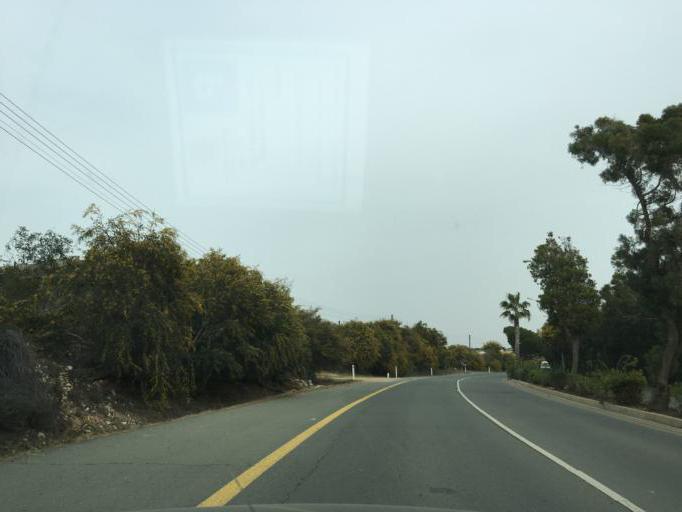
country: CY
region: Ammochostos
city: Ayia Napa
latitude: 34.9876
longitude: 34.0133
